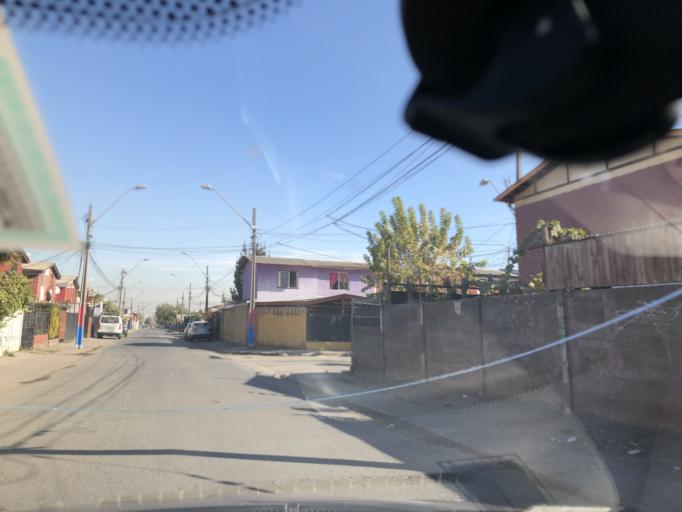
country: CL
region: Santiago Metropolitan
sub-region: Provincia de Cordillera
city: Puente Alto
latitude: -33.5854
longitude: -70.5982
